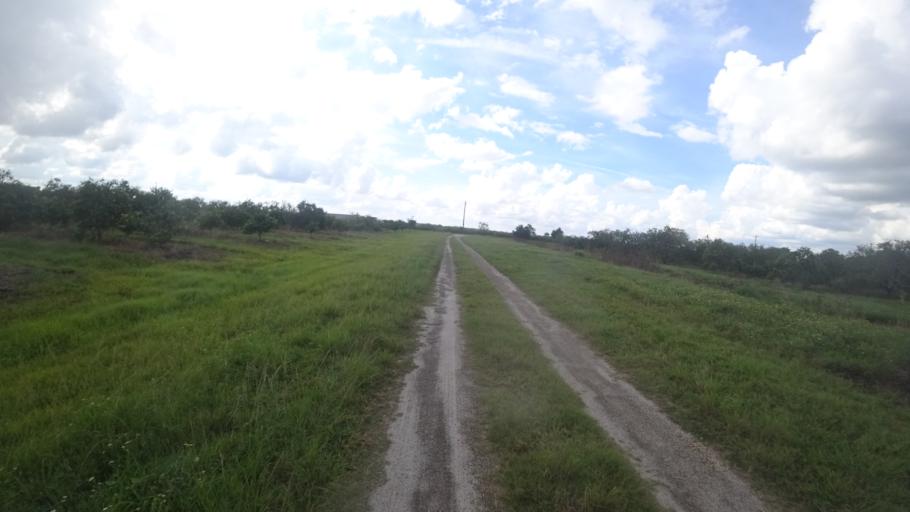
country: US
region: Florida
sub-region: Hillsborough County
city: Wimauma
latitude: 27.5741
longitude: -82.1035
